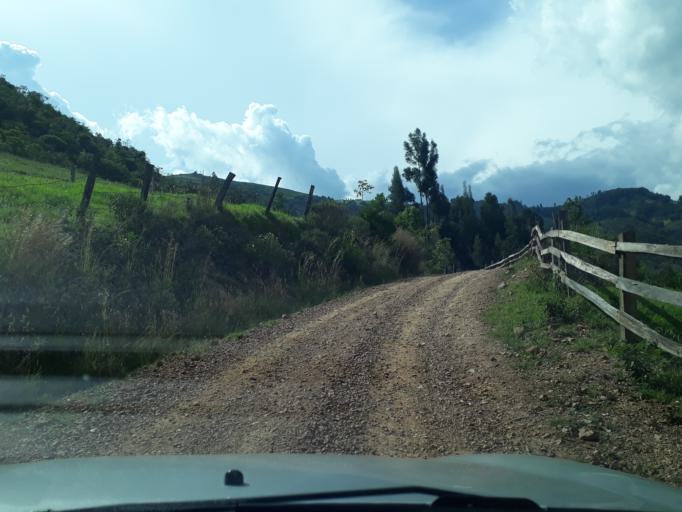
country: CO
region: Boyaca
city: Santa Rosa de Viterbo
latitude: 5.8526
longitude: -72.9669
